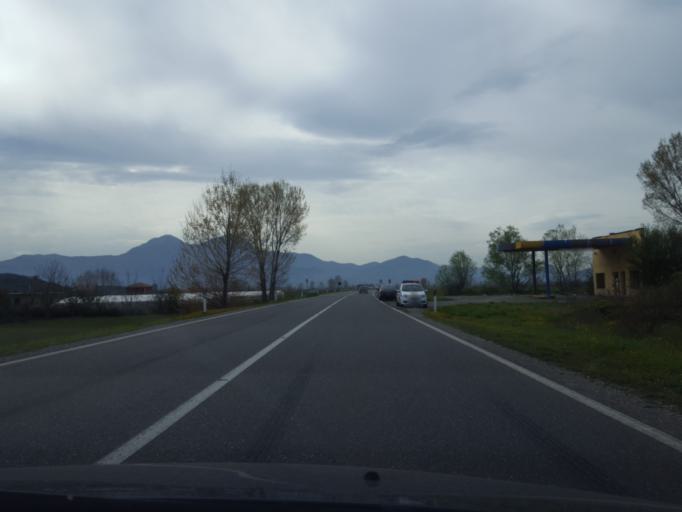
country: AL
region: Lezhe
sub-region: Rrethi i Lezhes
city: Dajc
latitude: 41.9104
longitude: 19.5993
